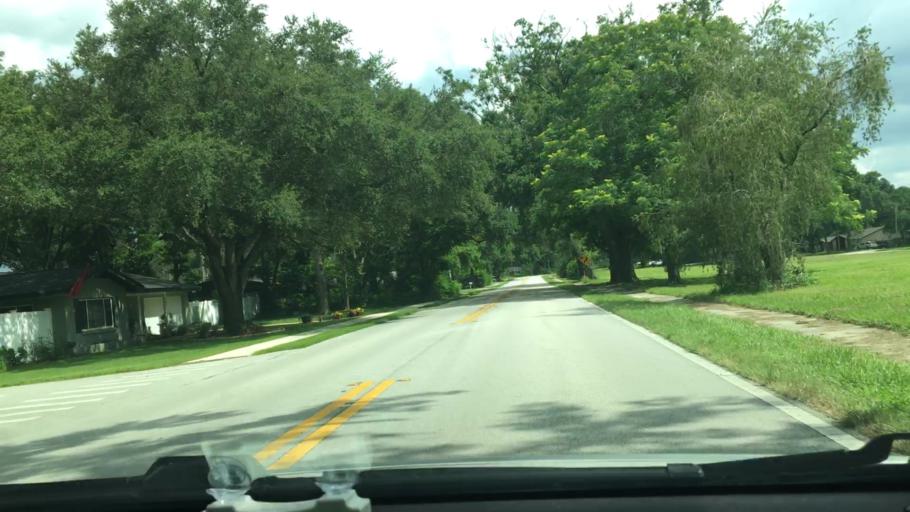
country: US
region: Florida
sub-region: Seminole County
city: Altamonte Springs
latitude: 28.6919
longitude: -81.3712
